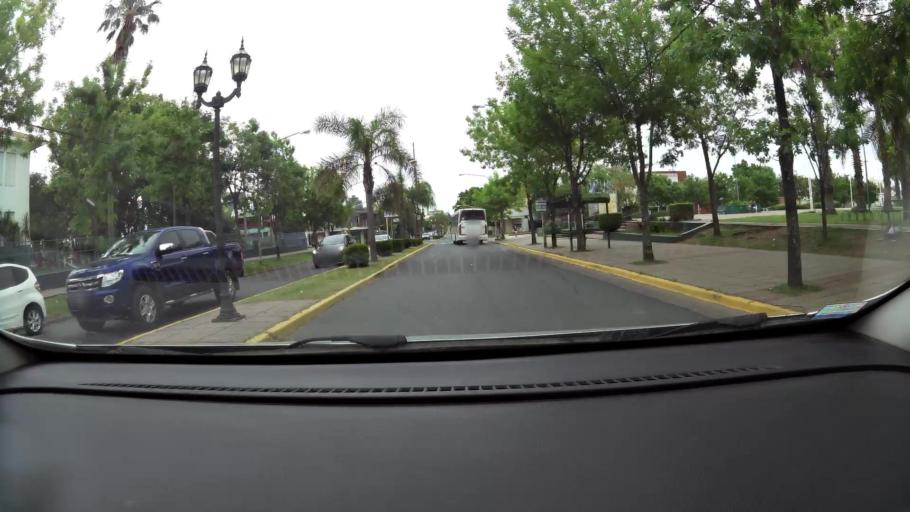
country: AR
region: Buenos Aires
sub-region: Partido de Campana
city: Campana
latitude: -34.1704
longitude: -58.9598
